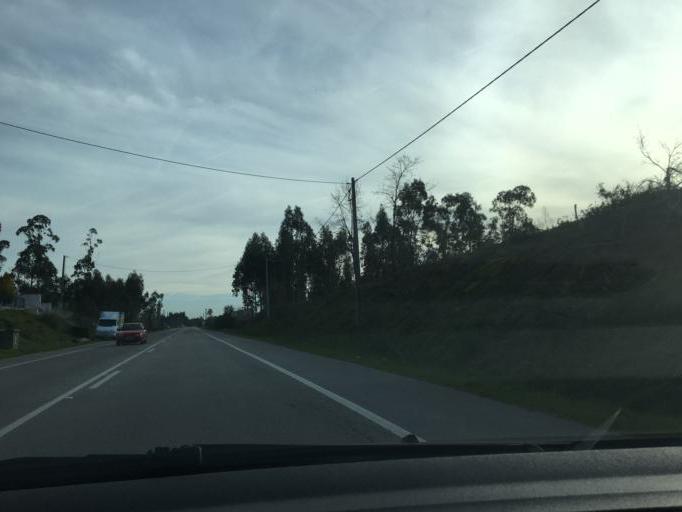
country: PT
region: Coimbra
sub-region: Soure
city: Alfarelos
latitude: 40.2143
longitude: -8.6081
